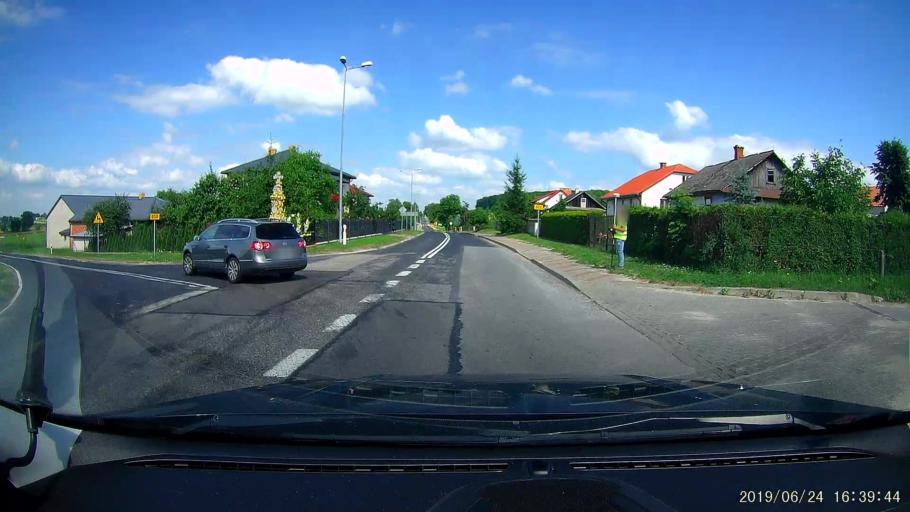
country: PL
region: Lublin Voivodeship
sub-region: Powiat tomaszowski
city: Rachanie
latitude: 50.5297
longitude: 23.5590
